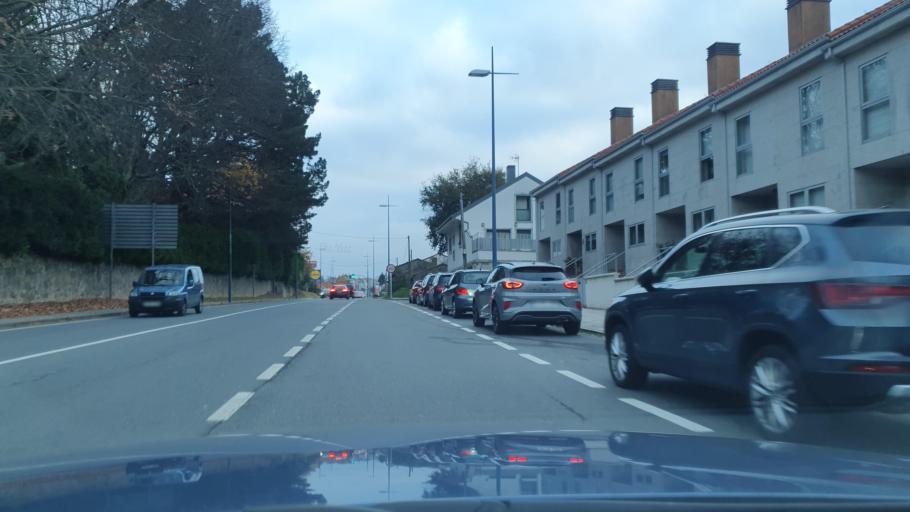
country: ES
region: Galicia
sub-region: Provincia da Coruna
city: Santiago de Compostela
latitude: 42.8646
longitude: -8.5665
